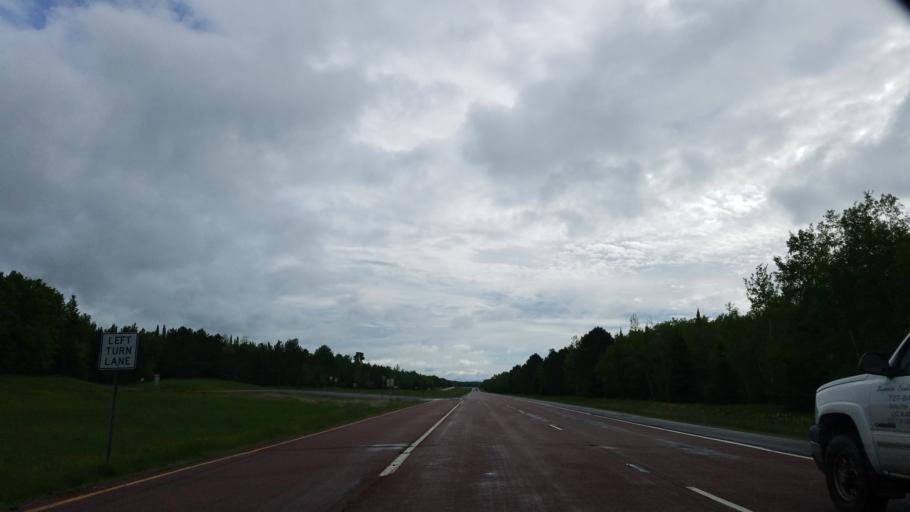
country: US
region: Minnesota
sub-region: Saint Louis County
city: Arnold
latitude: 46.9131
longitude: -91.8799
